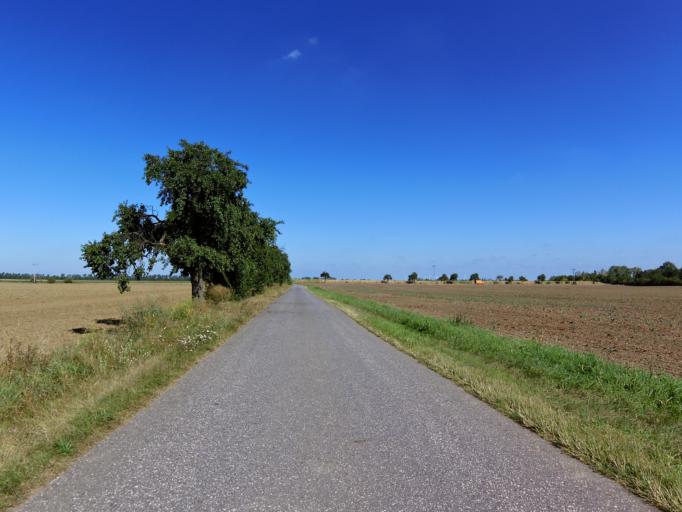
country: DE
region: Brandenburg
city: Muhlberg
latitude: 51.4017
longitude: 13.2432
